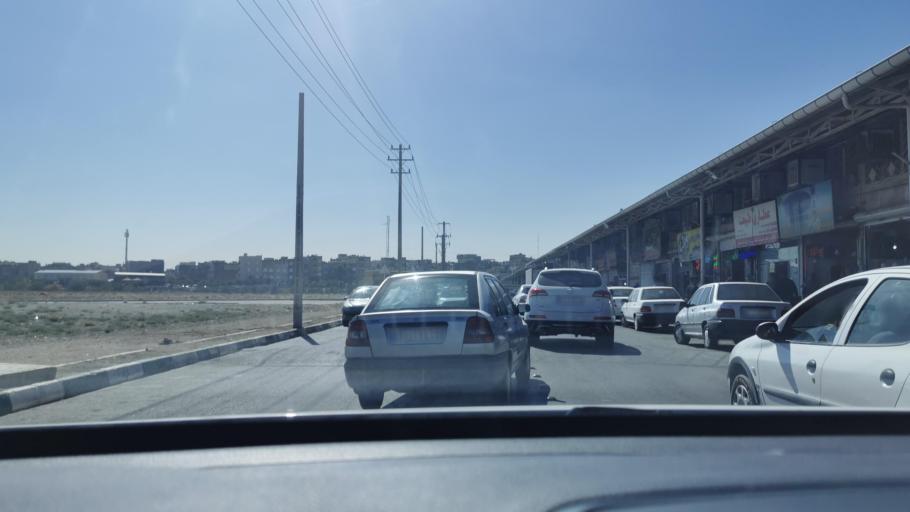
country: IR
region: Razavi Khorasan
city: Mashhad
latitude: 36.3359
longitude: 59.6196
